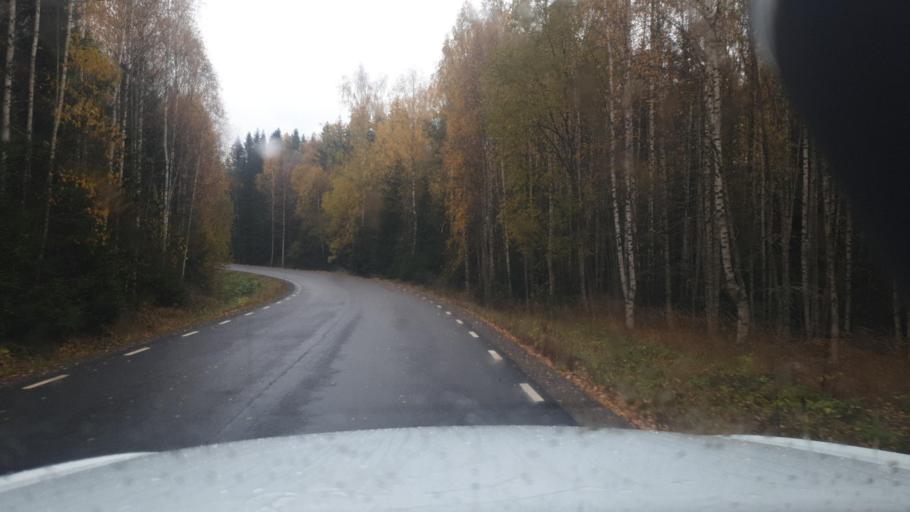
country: SE
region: Vaermland
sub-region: Torsby Kommun
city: Torsby
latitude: 60.0020
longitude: 12.7254
